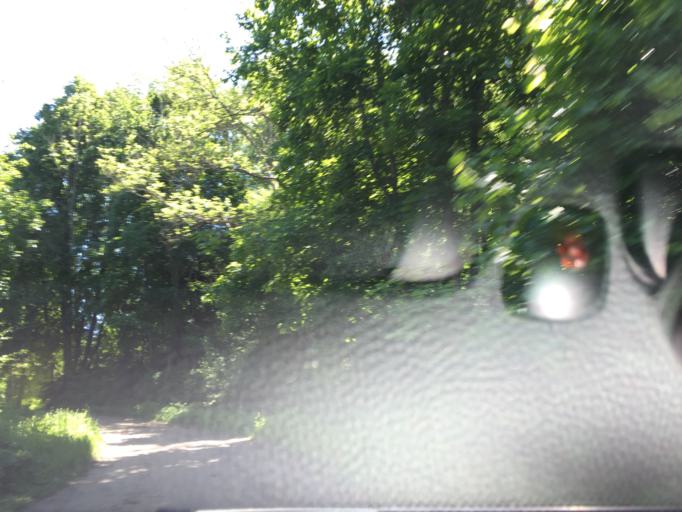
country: LV
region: Preilu Rajons
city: Jaunaglona
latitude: 56.2333
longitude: 27.2304
